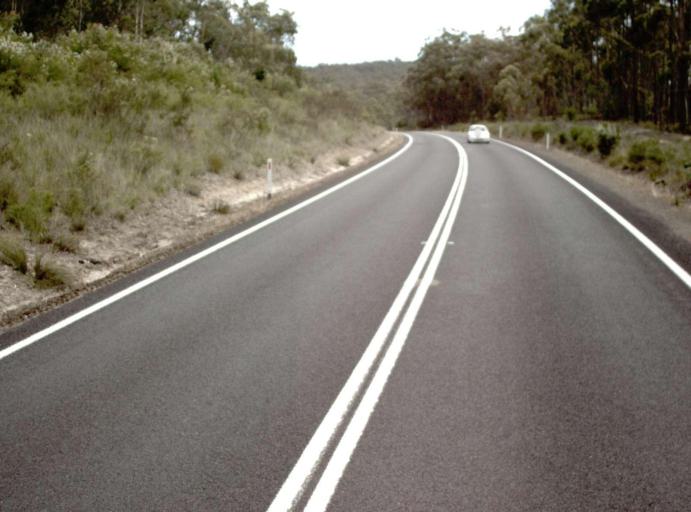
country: AU
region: New South Wales
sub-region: Bega Valley
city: Eden
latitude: -37.4842
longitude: 149.5511
